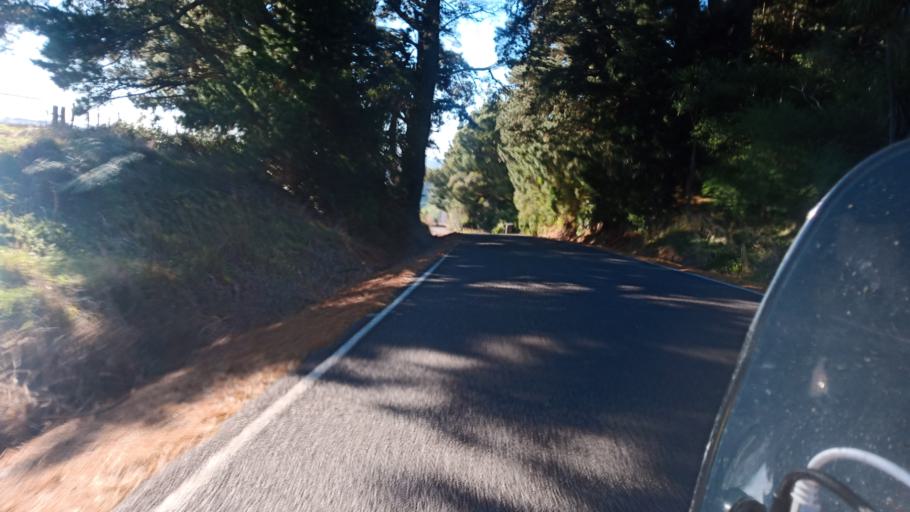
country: NZ
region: Hawke's Bay
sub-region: Wairoa District
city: Wairoa
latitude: -38.8328
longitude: 177.2715
